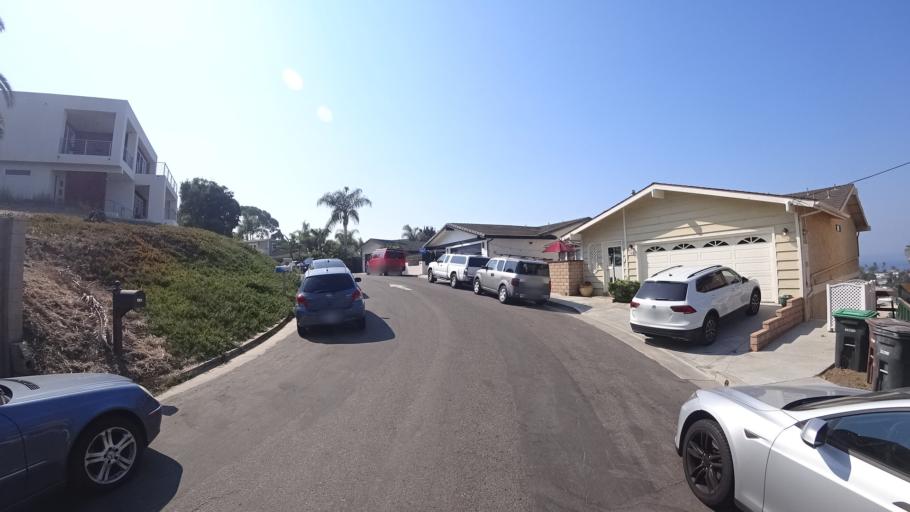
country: US
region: California
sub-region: Orange County
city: San Clemente
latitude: 33.4342
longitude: -117.6235
